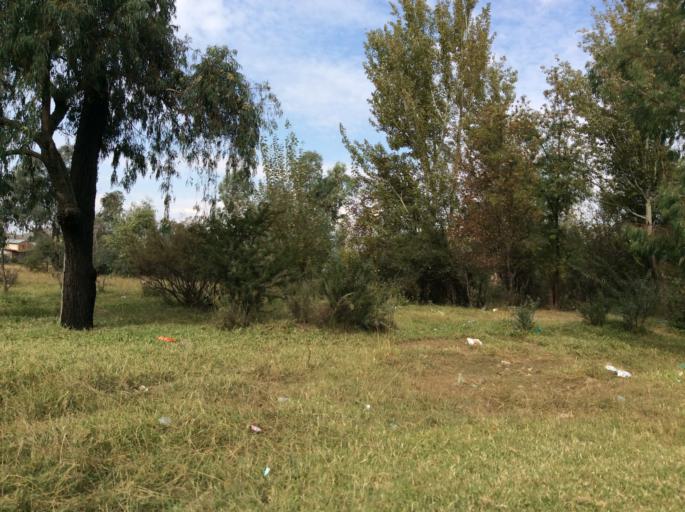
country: ZA
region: Orange Free State
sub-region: Xhariep District Municipality
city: Dewetsdorp
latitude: -29.5818
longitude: 26.6702
